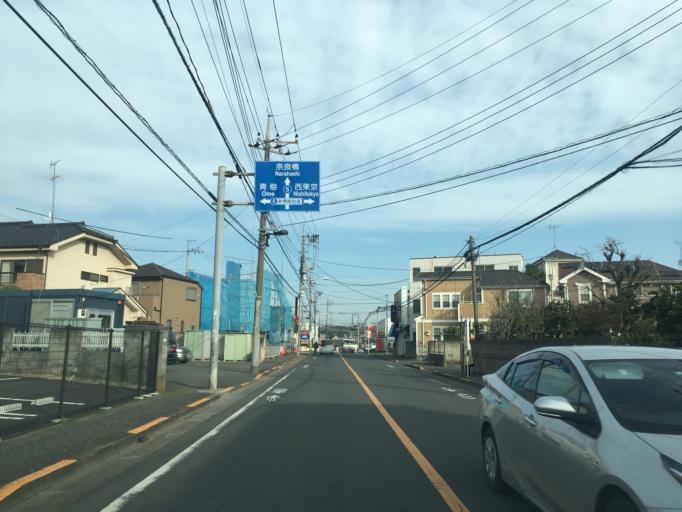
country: JP
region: Tokyo
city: Higashimurayama-shi
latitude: 35.7460
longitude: 139.4283
